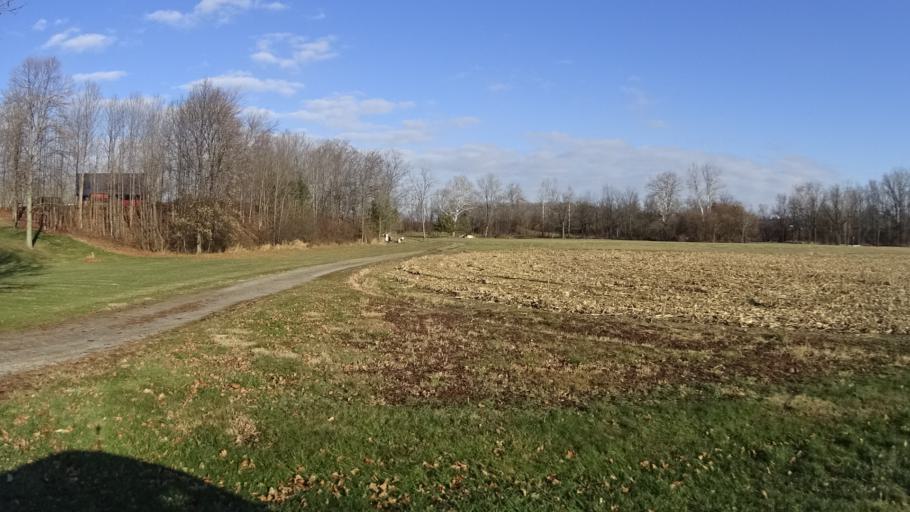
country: US
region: Ohio
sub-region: Lorain County
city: Oberlin
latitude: 41.2652
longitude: -82.1868
